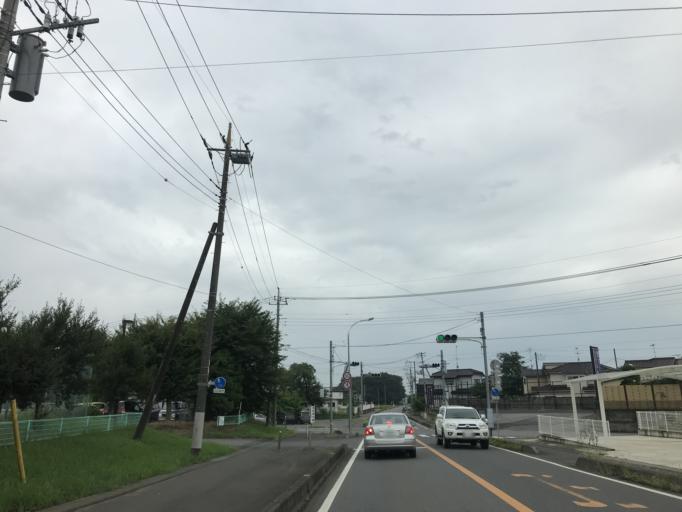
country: JP
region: Ibaraki
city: Sakai
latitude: 36.1210
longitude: 139.7920
